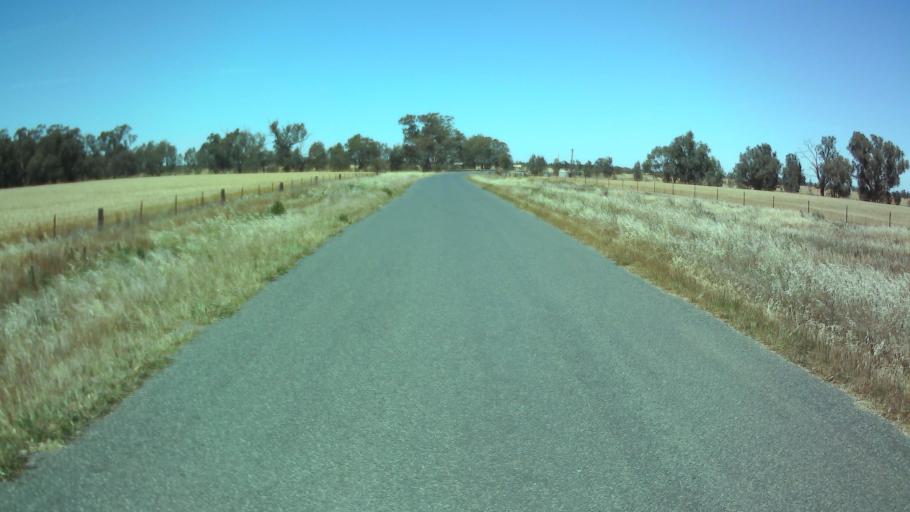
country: AU
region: New South Wales
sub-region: Weddin
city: Grenfell
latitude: -34.0371
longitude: 147.7898
